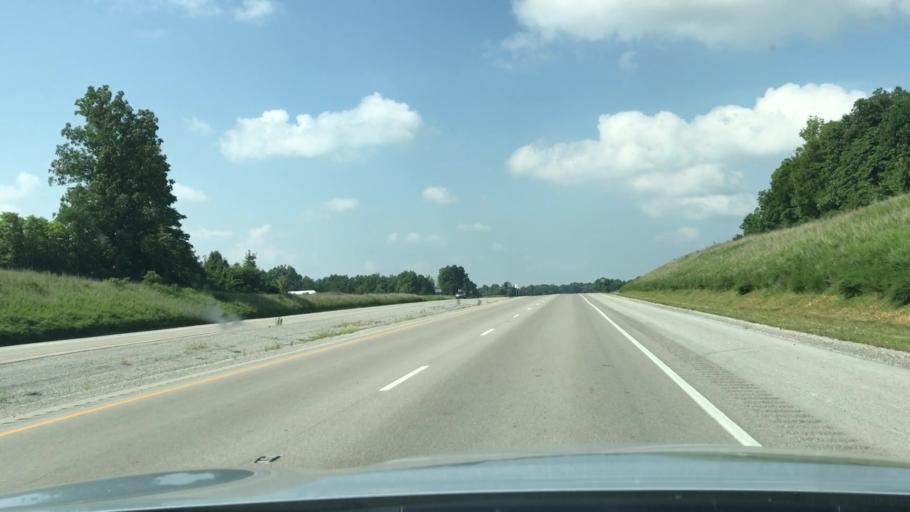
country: US
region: Kentucky
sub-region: Barren County
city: Glasgow
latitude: 37.0106
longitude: -85.9545
